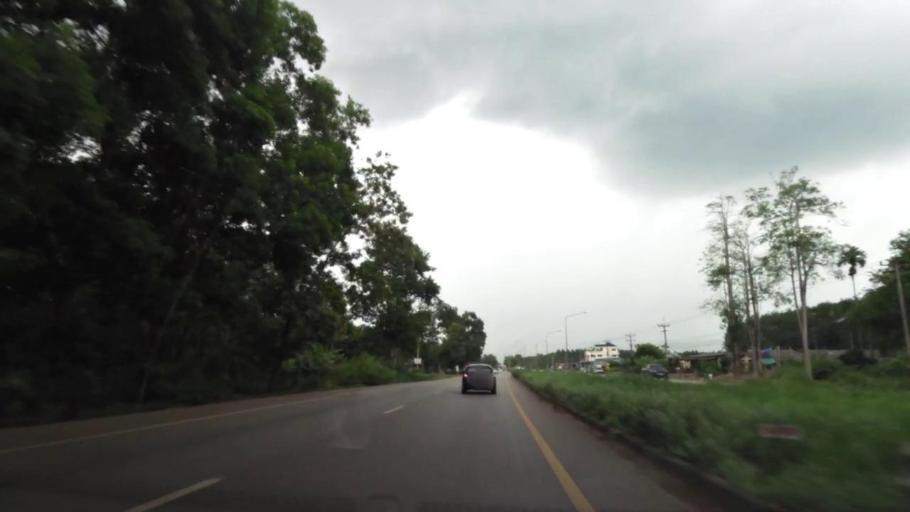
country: TH
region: Rayong
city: Wang Chan
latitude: 12.9726
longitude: 101.4944
